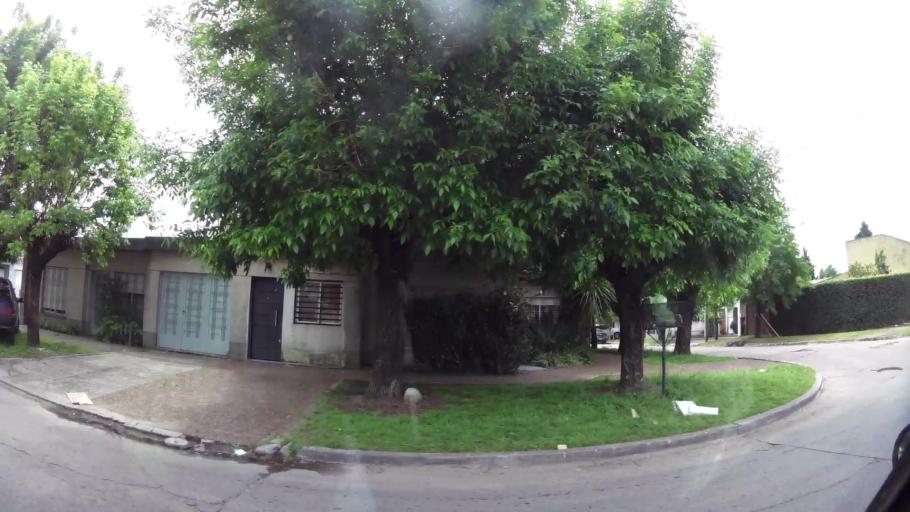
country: AR
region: Buenos Aires
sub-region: Partido de Quilmes
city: Quilmes
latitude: -34.7644
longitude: -58.2736
